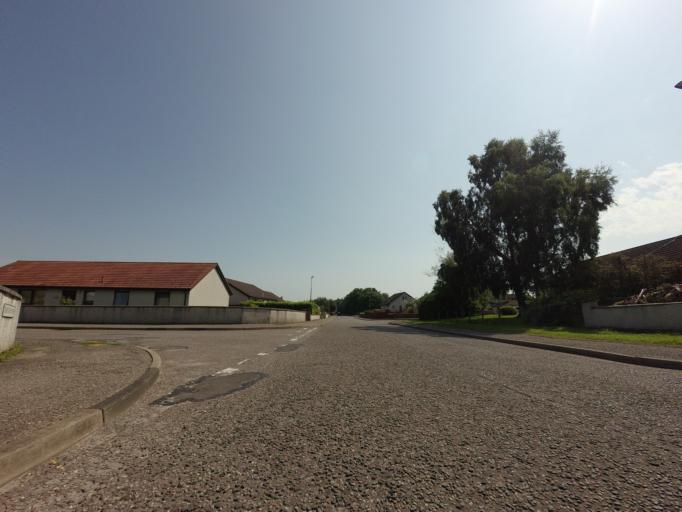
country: GB
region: Scotland
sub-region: Highland
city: Tain
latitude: 57.8052
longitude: -4.0597
